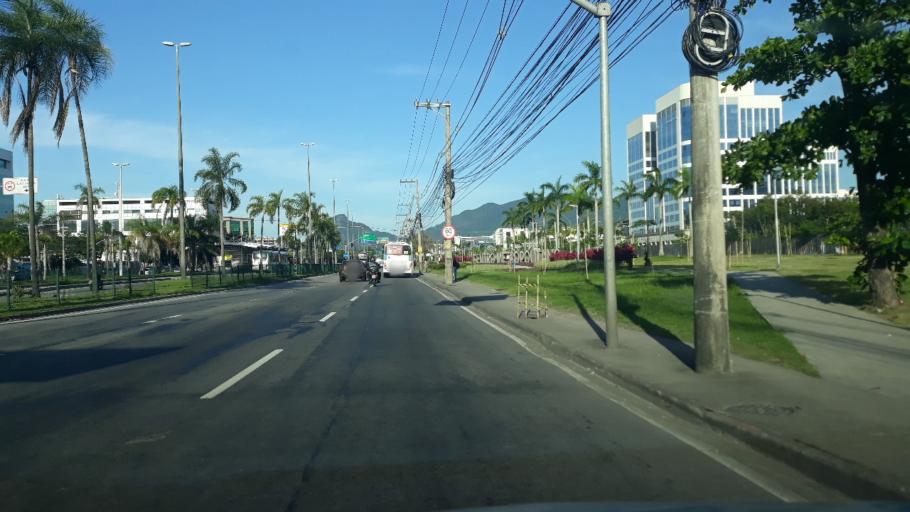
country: BR
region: Rio de Janeiro
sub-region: Sao Joao De Meriti
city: Sao Joao de Meriti
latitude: -22.9732
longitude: -43.3641
